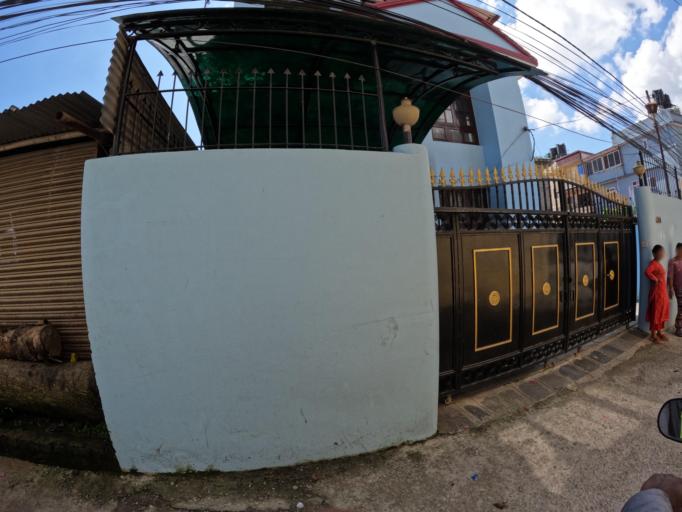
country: NP
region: Central Region
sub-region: Bagmati Zone
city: Kathmandu
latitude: 27.7458
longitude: 85.3318
